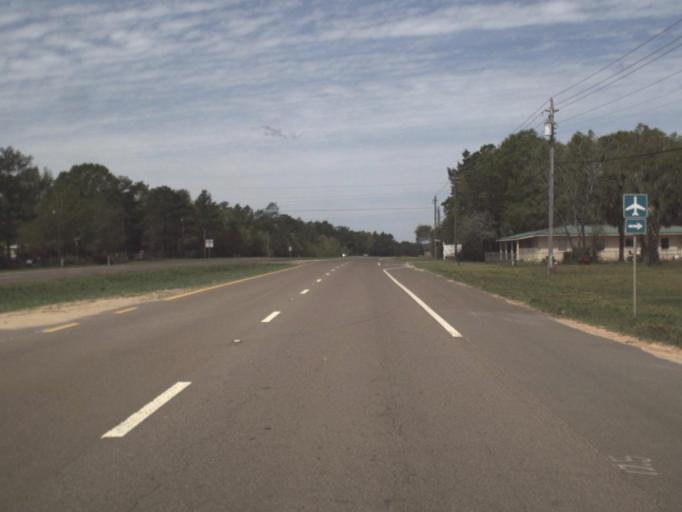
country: US
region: Florida
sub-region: Okaloosa County
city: Crestview
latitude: 30.7557
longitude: -86.5271
